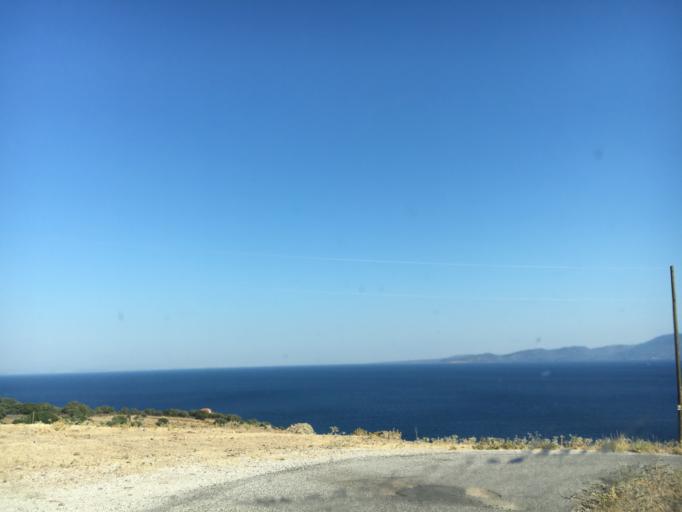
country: TR
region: Canakkale
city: Behram
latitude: 39.4862
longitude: 26.2694
